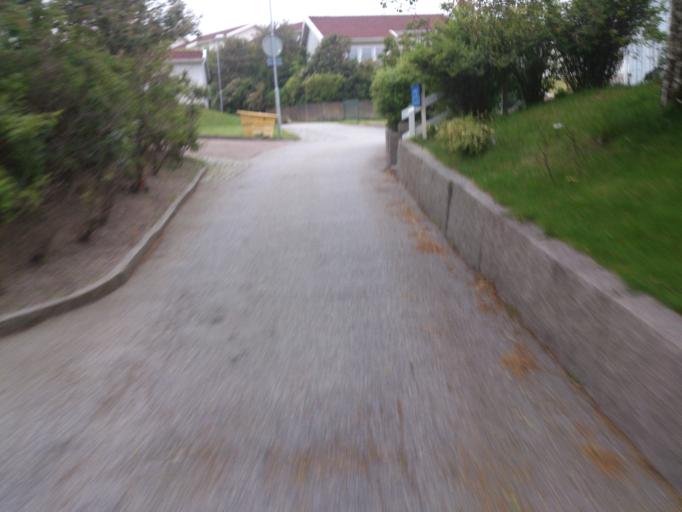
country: SE
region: Vaestra Goetaland
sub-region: Sotenas Kommun
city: Kungshamn
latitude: 58.3784
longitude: 11.2613
